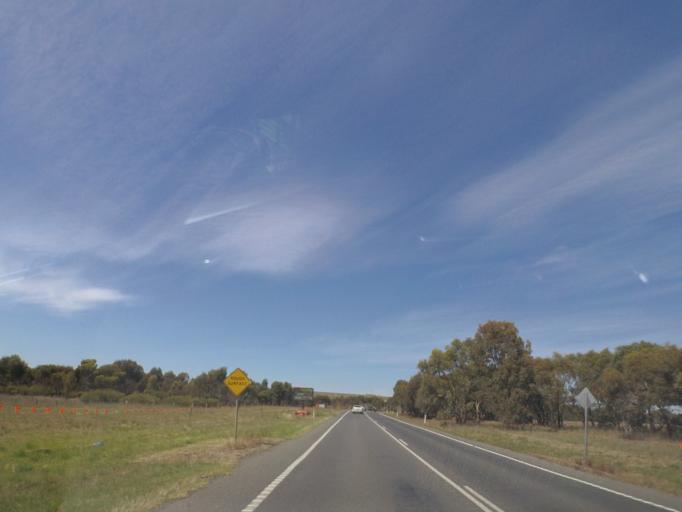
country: AU
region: Victoria
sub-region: Greater Geelong
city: Lara
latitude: -37.8830
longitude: 144.3784
